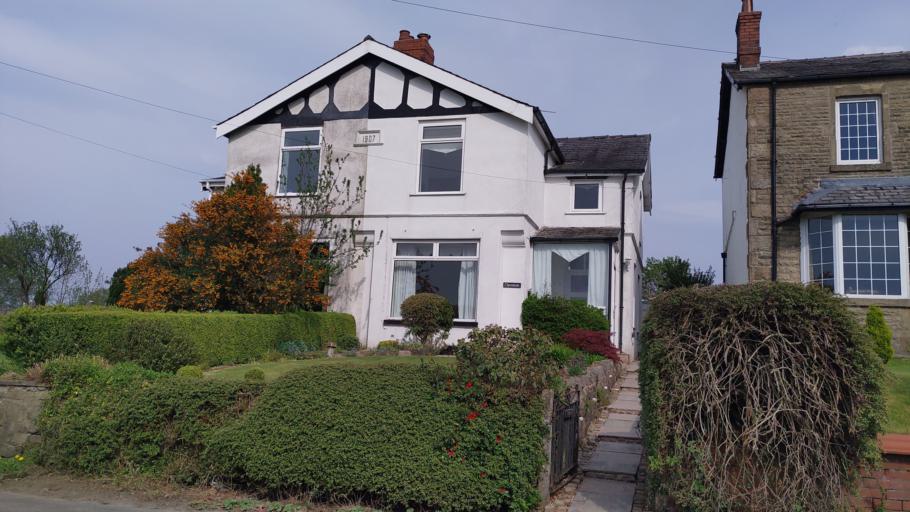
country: GB
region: England
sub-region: Lancashire
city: Chorley
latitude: 53.6707
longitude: -2.5908
